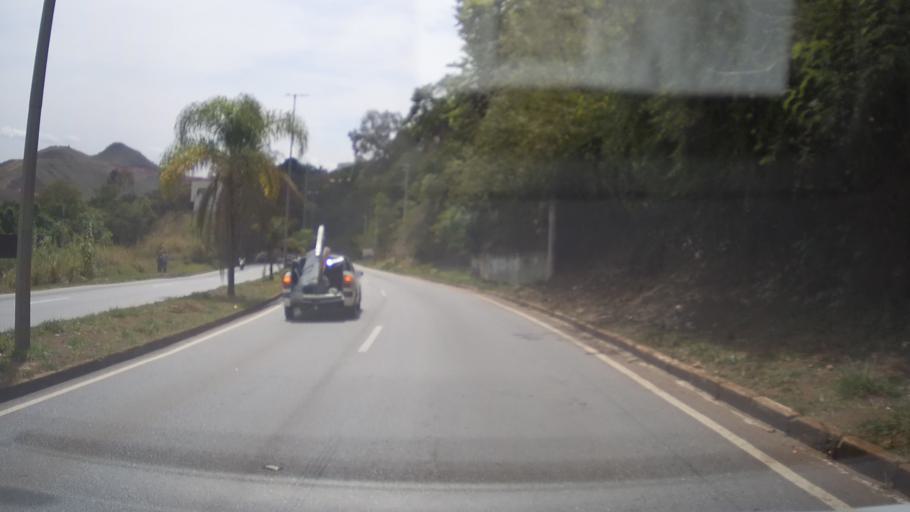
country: BR
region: Minas Gerais
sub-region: Belo Horizonte
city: Belo Horizonte
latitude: -19.9875
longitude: -43.9365
